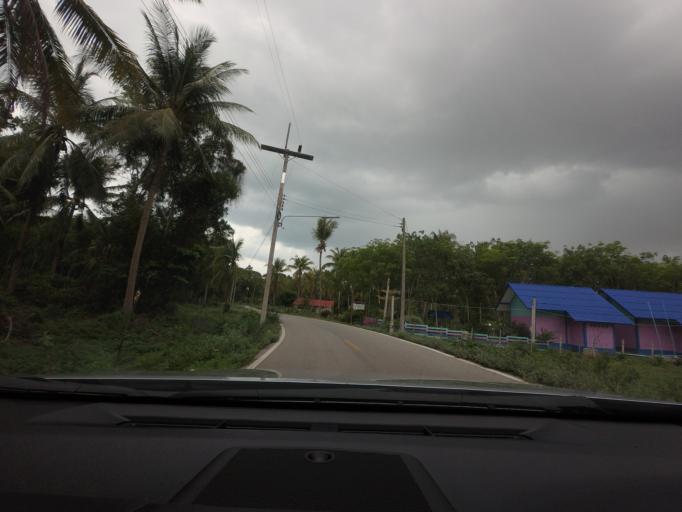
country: TH
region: Songkhla
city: Chana
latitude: 6.9538
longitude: 100.8400
